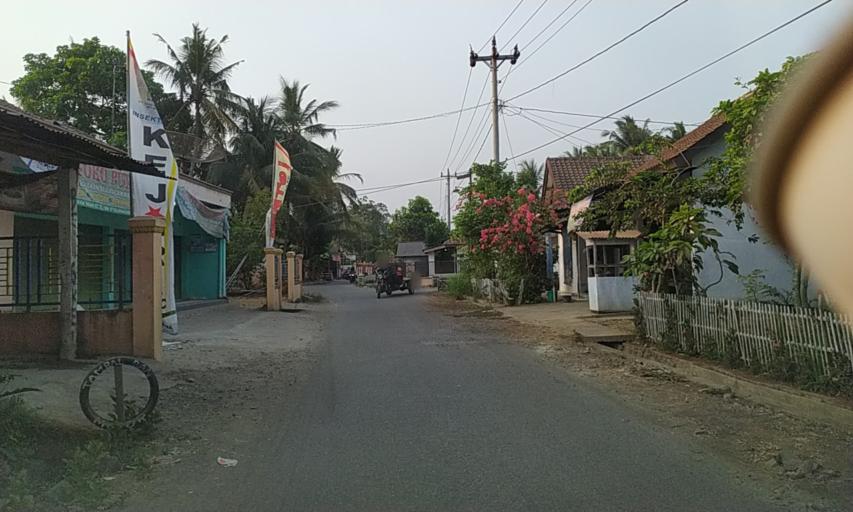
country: ID
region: Central Java
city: Bojongsari
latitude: -7.3117
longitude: 108.7639
